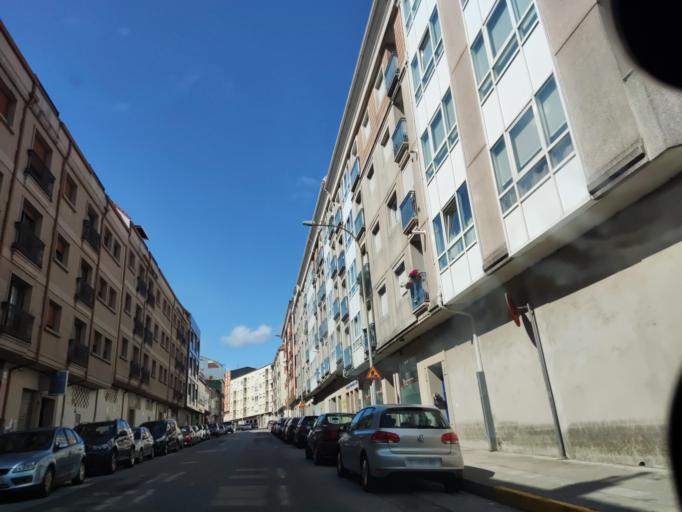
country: ES
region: Galicia
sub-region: Provincia da Coruna
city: Boiro
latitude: 42.6438
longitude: -8.8828
